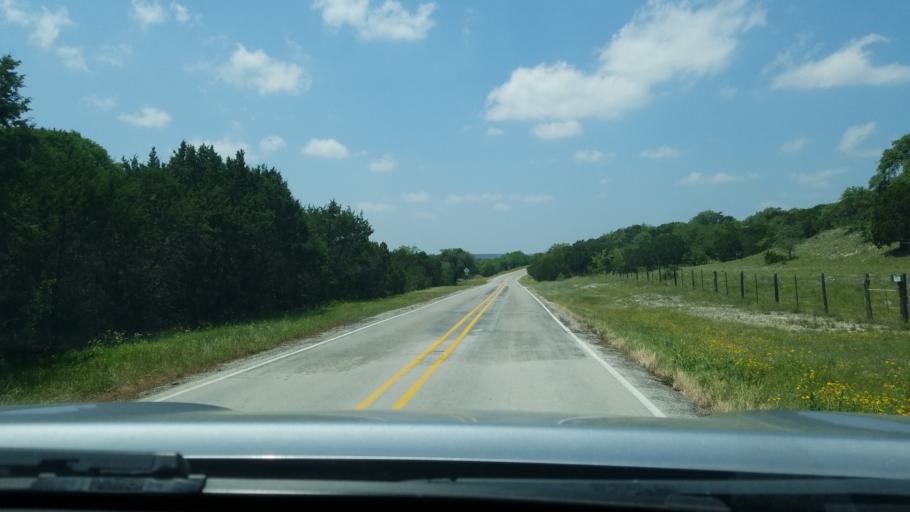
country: US
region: Texas
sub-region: Hays County
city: Woodcreek
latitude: 30.0930
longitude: -98.2319
